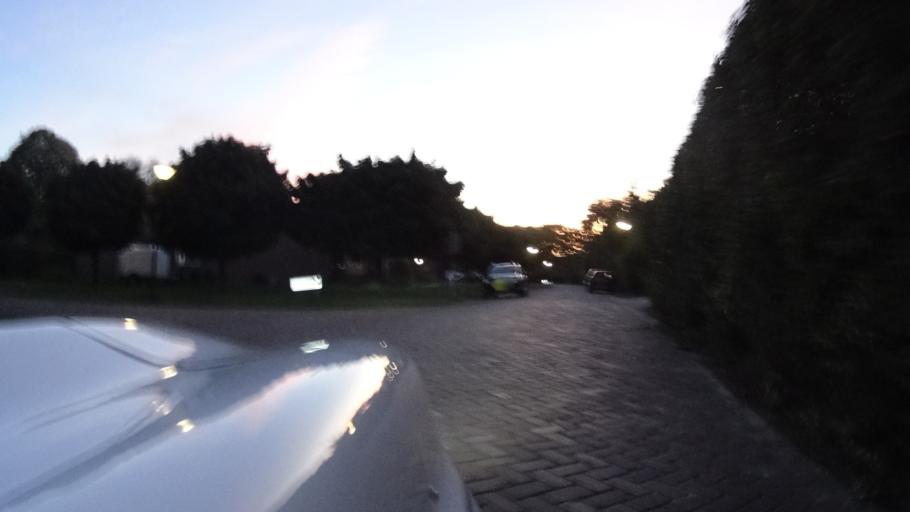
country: NL
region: North Brabant
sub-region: Gemeente Aalburg
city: Aalburg
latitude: 51.7387
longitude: 5.0930
